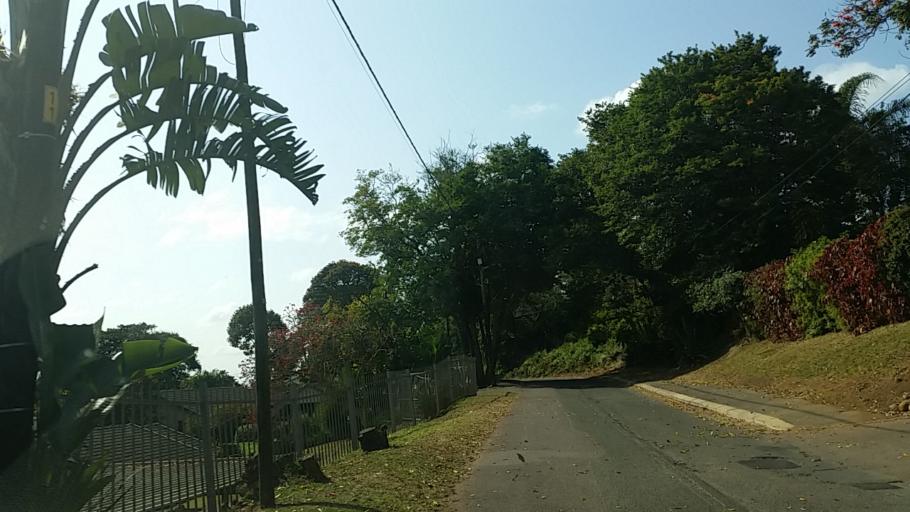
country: ZA
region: KwaZulu-Natal
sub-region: eThekwini Metropolitan Municipality
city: Berea
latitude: -29.8350
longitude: 30.9062
